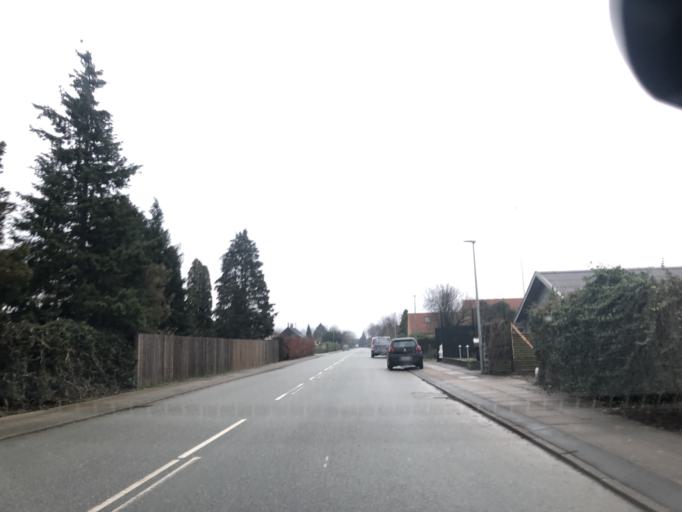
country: DK
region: Capital Region
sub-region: Tarnby Kommune
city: Tarnby
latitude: 55.6378
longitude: 12.5960
